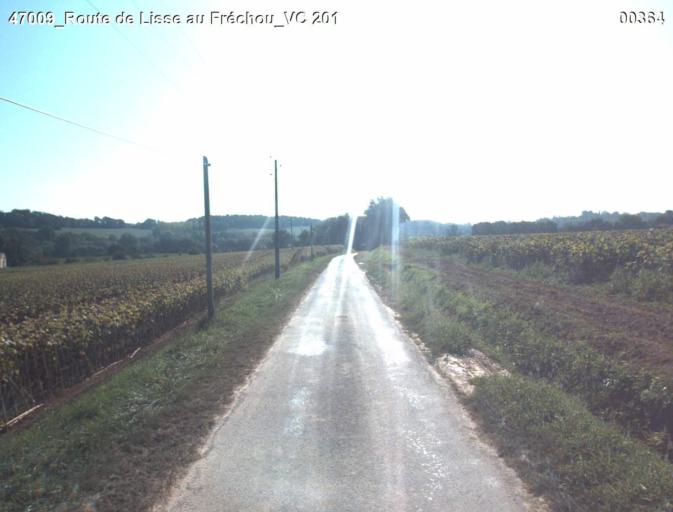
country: FR
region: Aquitaine
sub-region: Departement du Lot-et-Garonne
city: Nerac
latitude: 44.0938
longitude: 0.3062
